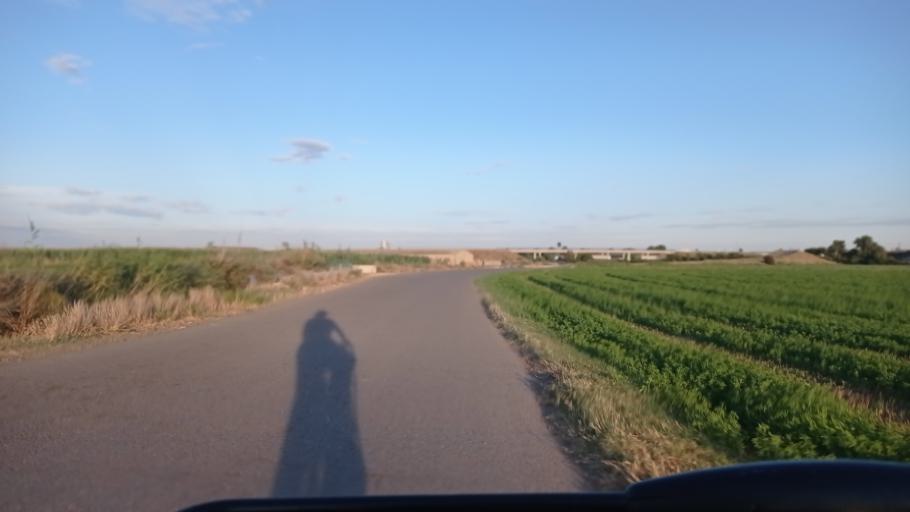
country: ES
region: Aragon
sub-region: Provincia de Zaragoza
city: Oliver-Valdefierro, Oliver, Valdefierro
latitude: 41.6805
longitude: -0.9326
